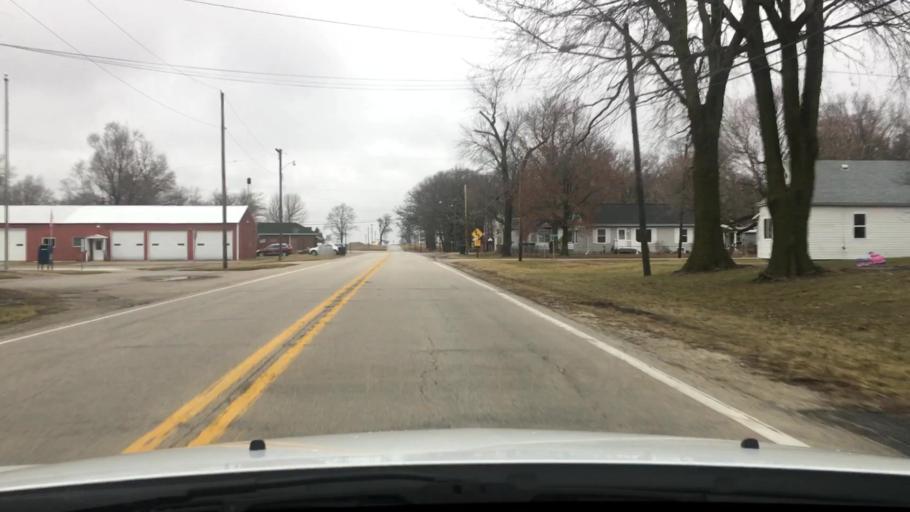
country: US
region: Illinois
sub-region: Iroquois County
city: Sheldon
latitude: 40.8260
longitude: -87.5816
